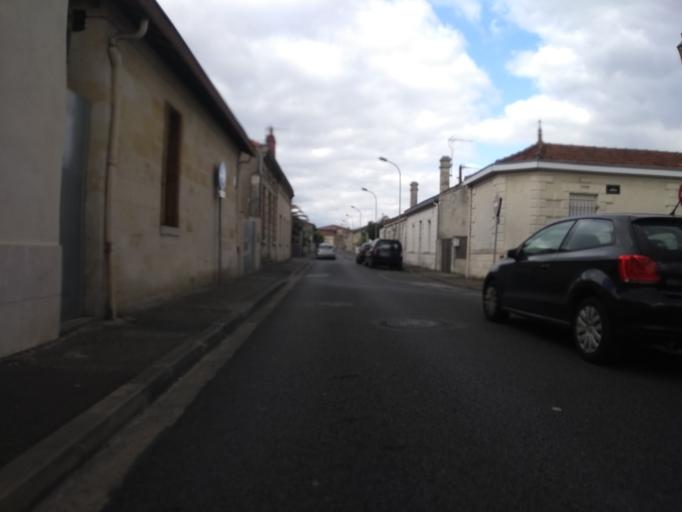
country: FR
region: Aquitaine
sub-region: Departement de la Gironde
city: Begles
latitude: 44.8061
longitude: -0.5663
